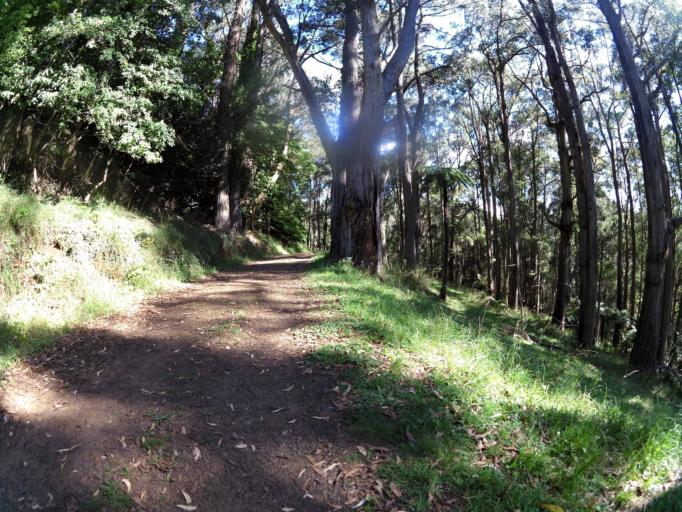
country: AU
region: Victoria
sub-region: Yarra Ranges
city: Ferny Creek
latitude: -37.8695
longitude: 145.3389
